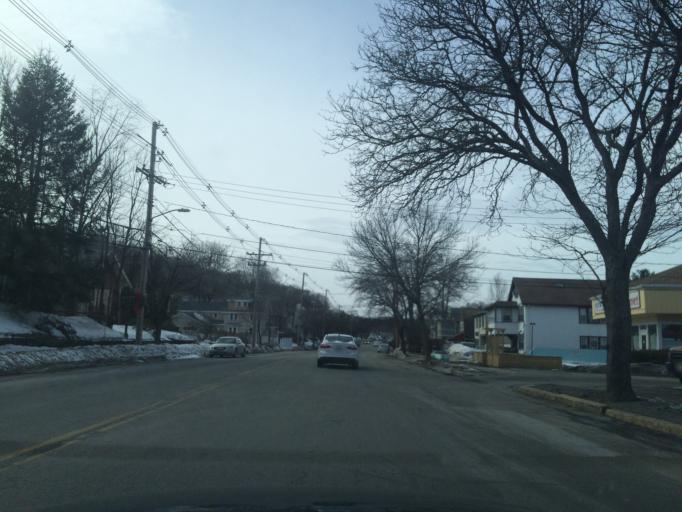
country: US
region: Massachusetts
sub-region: Middlesex County
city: Belmont
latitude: 42.4261
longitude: -71.1962
